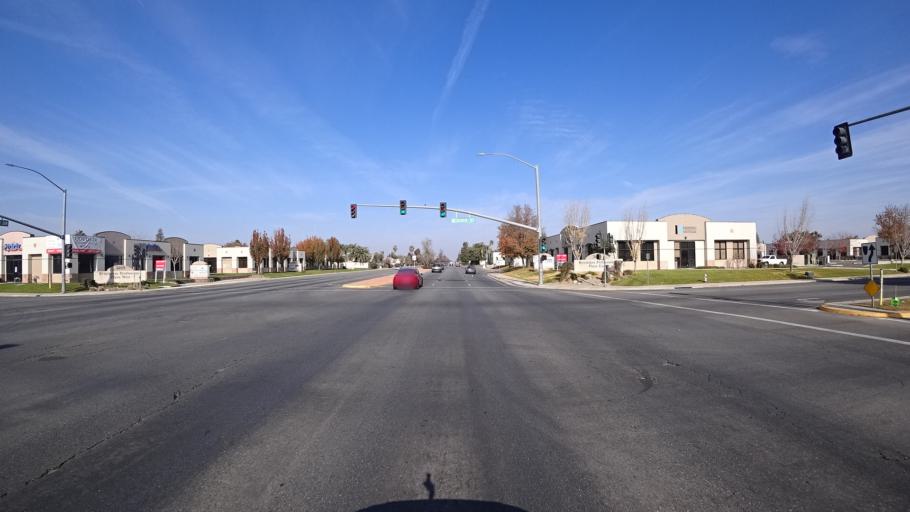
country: US
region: California
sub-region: Kern County
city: Greenacres
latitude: 35.3906
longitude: -119.1099
